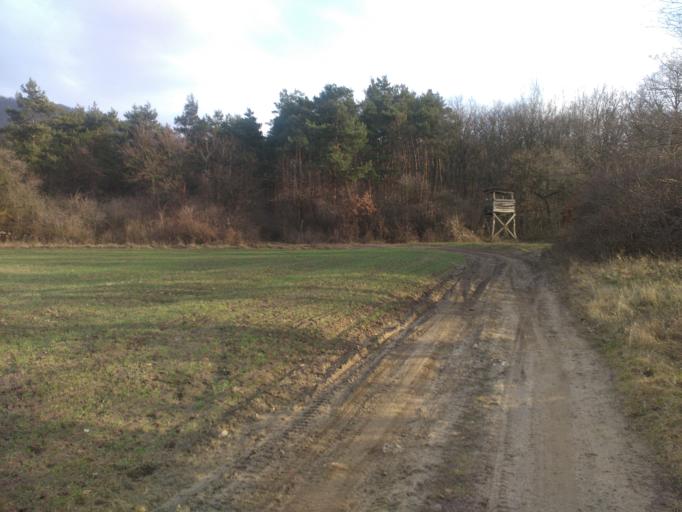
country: HU
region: Komarom-Esztergom
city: Piliscsev
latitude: 47.6697
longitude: 18.8291
